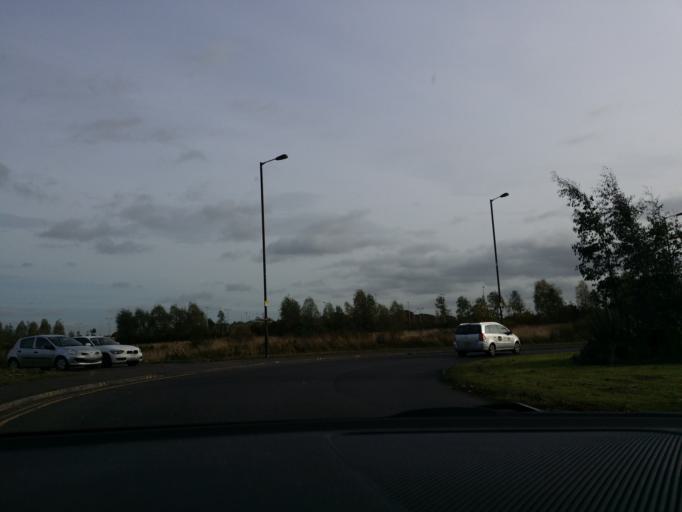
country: GB
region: Scotland
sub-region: Edinburgh
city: Ratho
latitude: 55.9403
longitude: -3.3591
